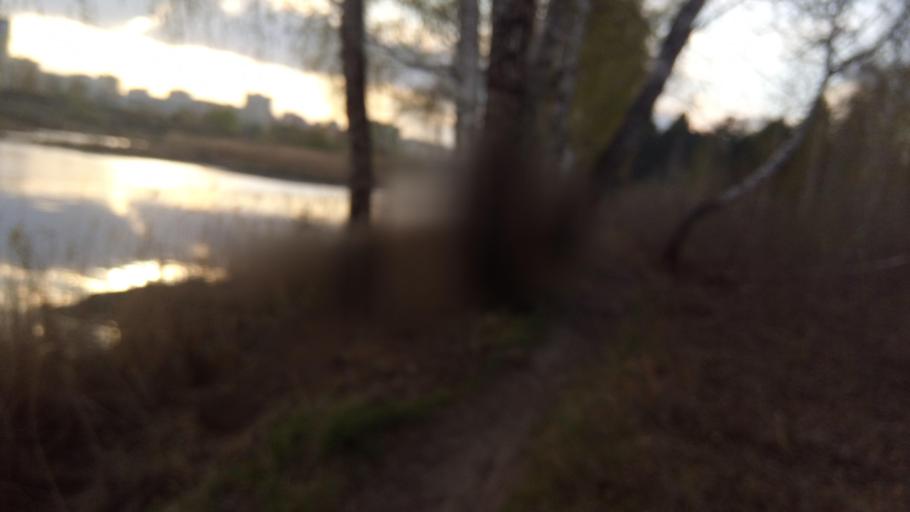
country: RU
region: Chelyabinsk
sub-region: Gorod Chelyabinsk
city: Chelyabinsk
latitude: 55.1594
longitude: 61.3166
